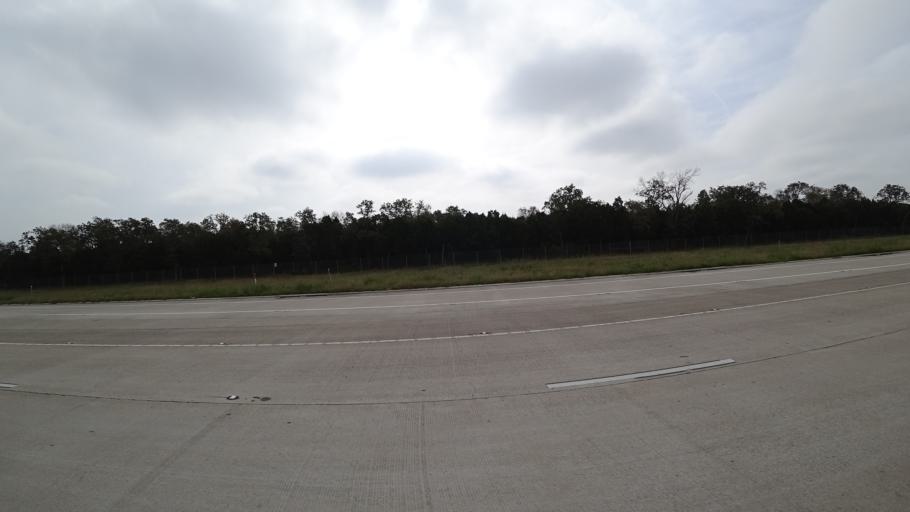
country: US
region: Texas
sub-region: Williamson County
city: Brushy Creek
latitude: 30.4781
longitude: -97.7242
